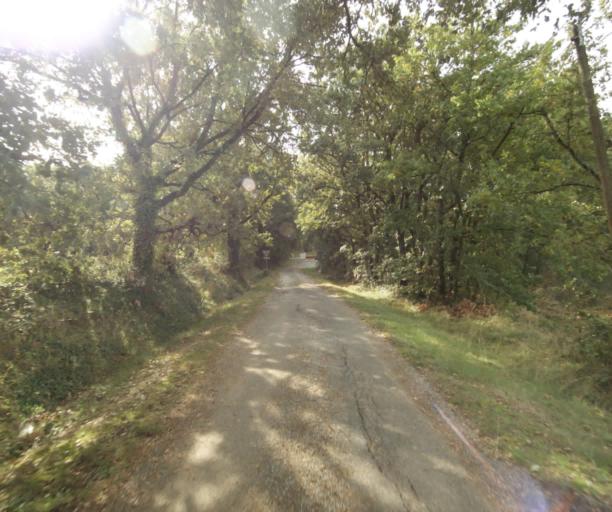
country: FR
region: Midi-Pyrenees
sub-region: Departement du Tarn-et-Garonne
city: Labastide-Saint-Pierre
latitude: 43.9083
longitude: 1.3841
